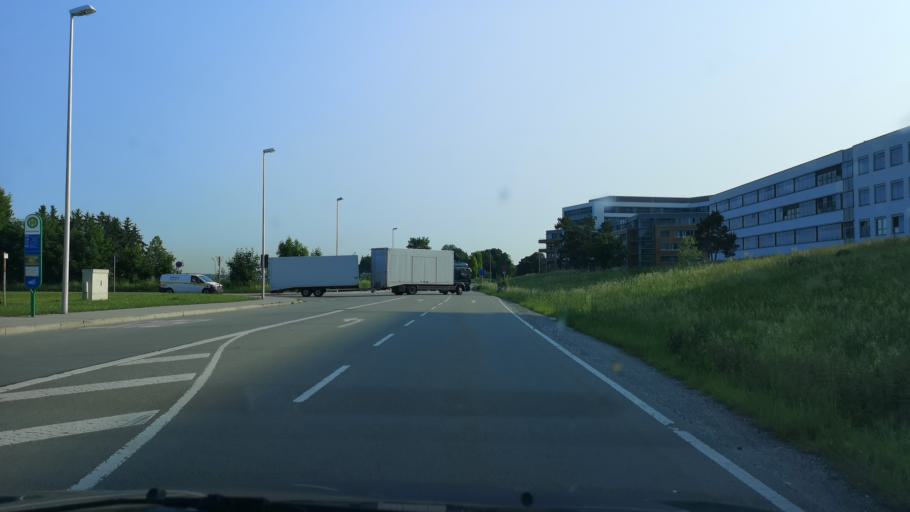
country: DE
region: Bavaria
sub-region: Upper Bavaria
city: Garching bei Munchen
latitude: 48.2507
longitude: 11.6312
